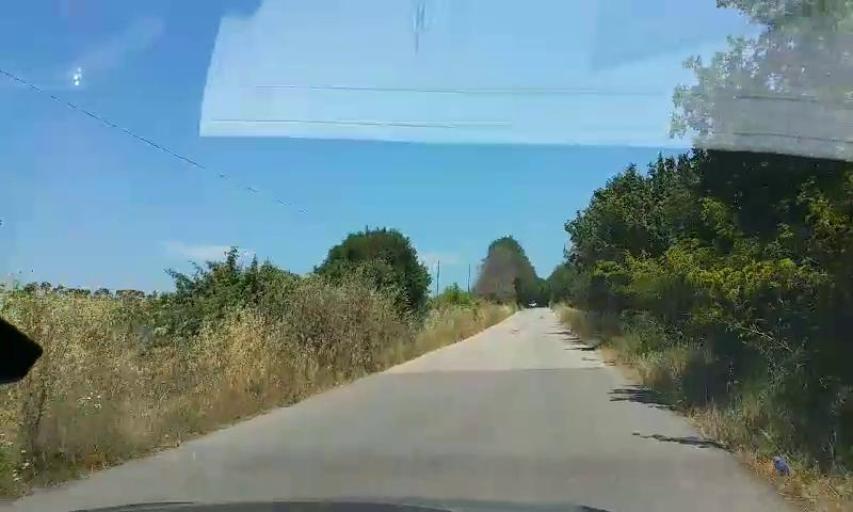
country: IT
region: Molise
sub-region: Provincia di Campobasso
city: Guglionesi
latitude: 41.9582
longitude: 14.9002
